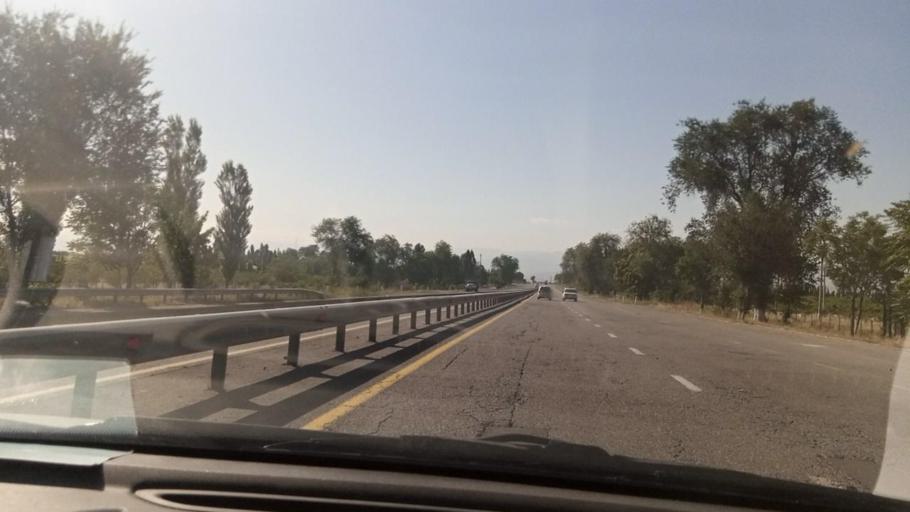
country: UZ
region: Toshkent
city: Ohangaron
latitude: 40.9376
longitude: 69.5859
